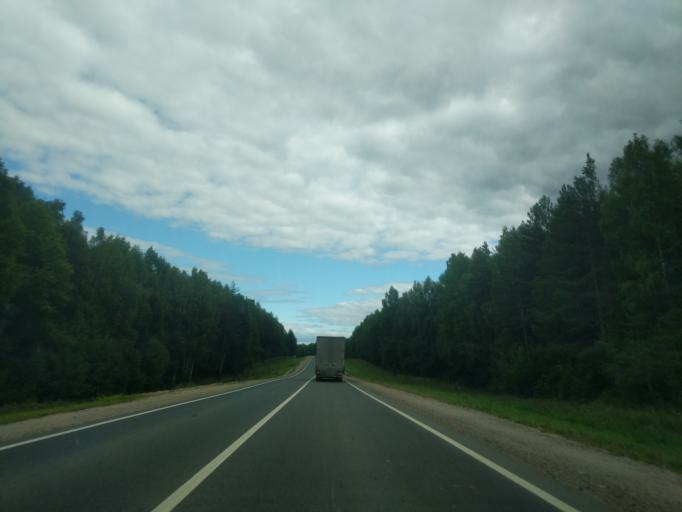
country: RU
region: Kostroma
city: Ostrovskoye
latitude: 57.8180
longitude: 42.2057
